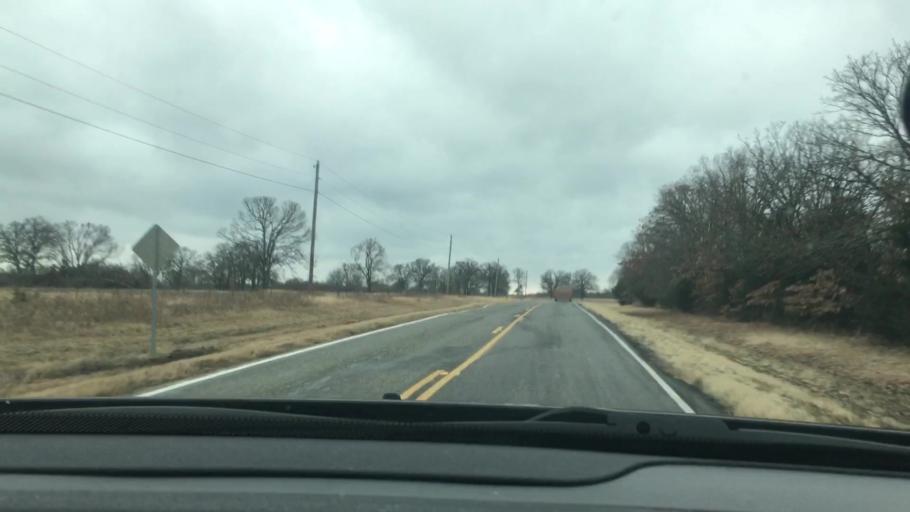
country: US
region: Oklahoma
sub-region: Johnston County
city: Tishomingo
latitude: 34.1881
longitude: -96.5793
